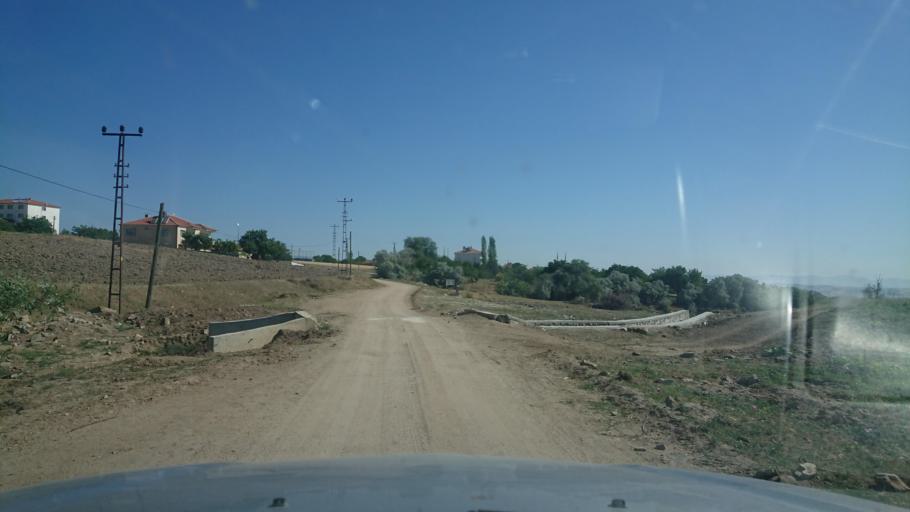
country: TR
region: Aksaray
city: Agacoren
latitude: 38.8628
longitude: 33.9126
